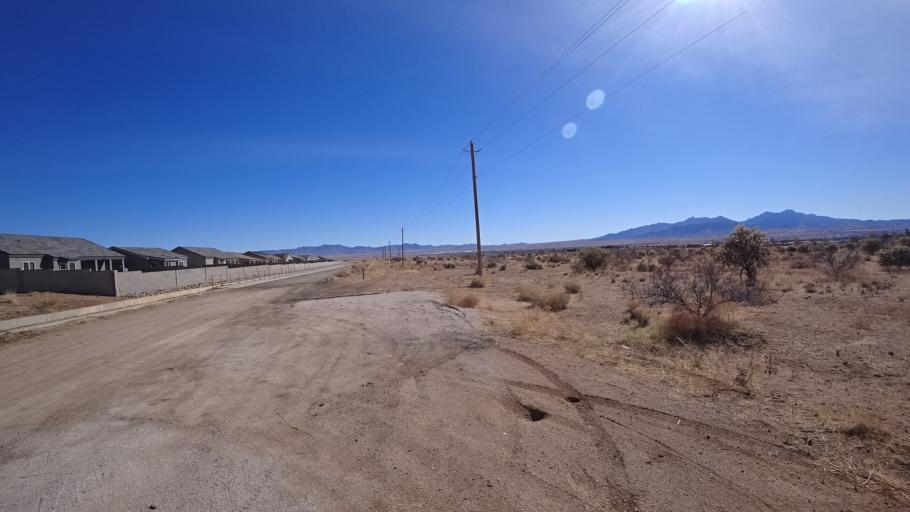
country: US
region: Arizona
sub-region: Mohave County
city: New Kingman-Butler
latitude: 35.2759
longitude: -114.0387
